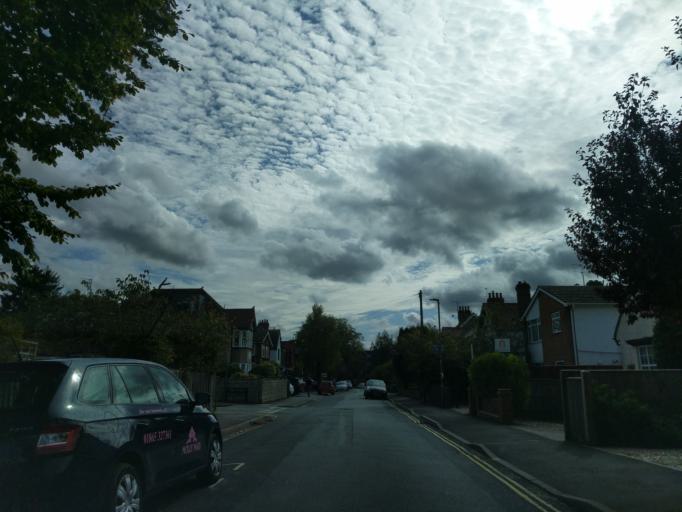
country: GB
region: England
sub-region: Oxfordshire
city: Cowley
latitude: 51.7598
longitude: -1.2182
